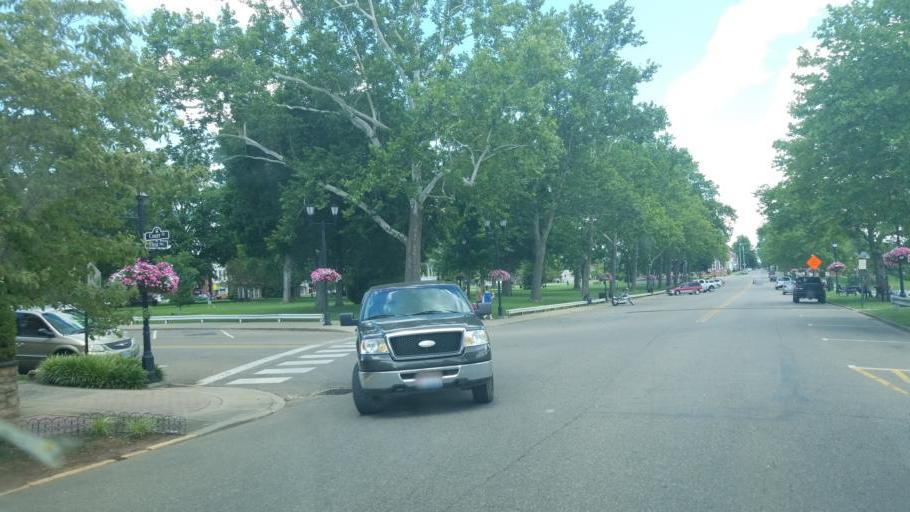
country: US
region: Ohio
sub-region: Gallia County
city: Gallipolis
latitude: 38.8056
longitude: -82.2066
